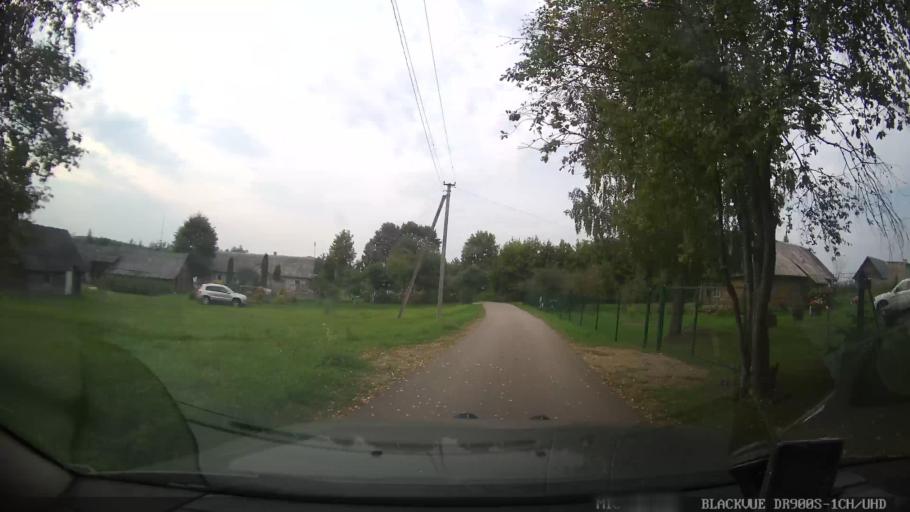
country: BY
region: Grodnenskaya
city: Ashmyany
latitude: 54.5307
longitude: 25.6696
